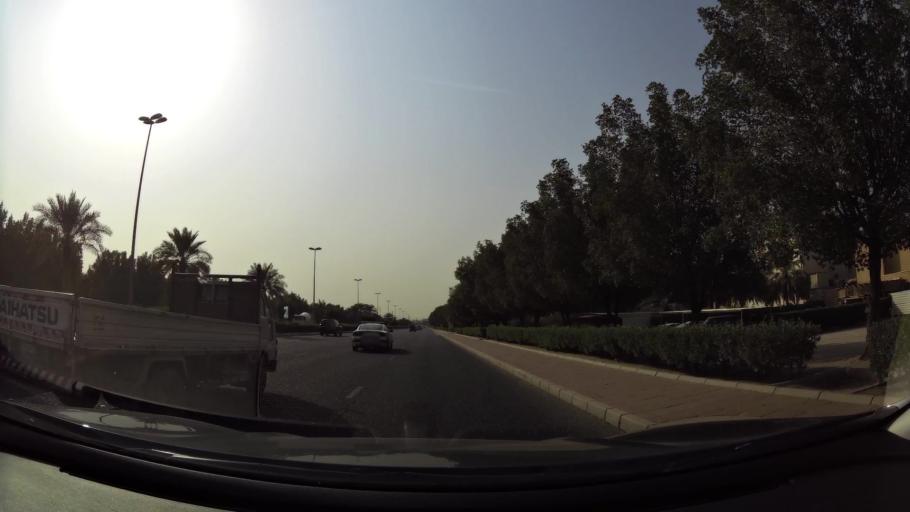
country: KW
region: Mubarak al Kabir
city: Mubarak al Kabir
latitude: 29.2091
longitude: 48.0851
